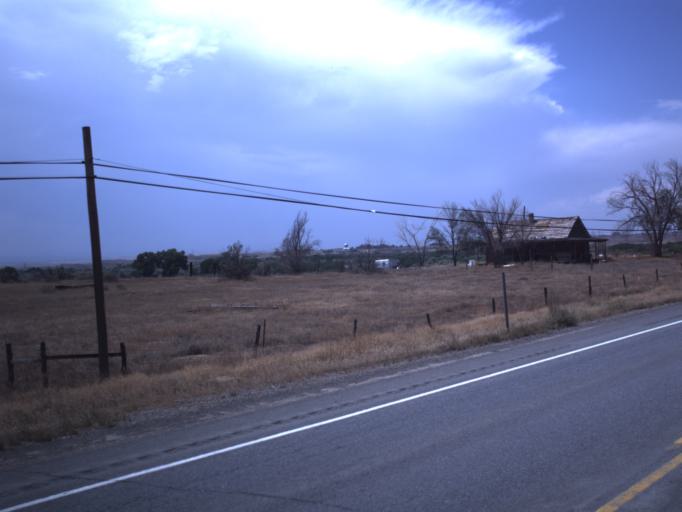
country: US
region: Utah
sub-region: Duchesne County
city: Roosevelt
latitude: 40.3020
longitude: -109.8330
